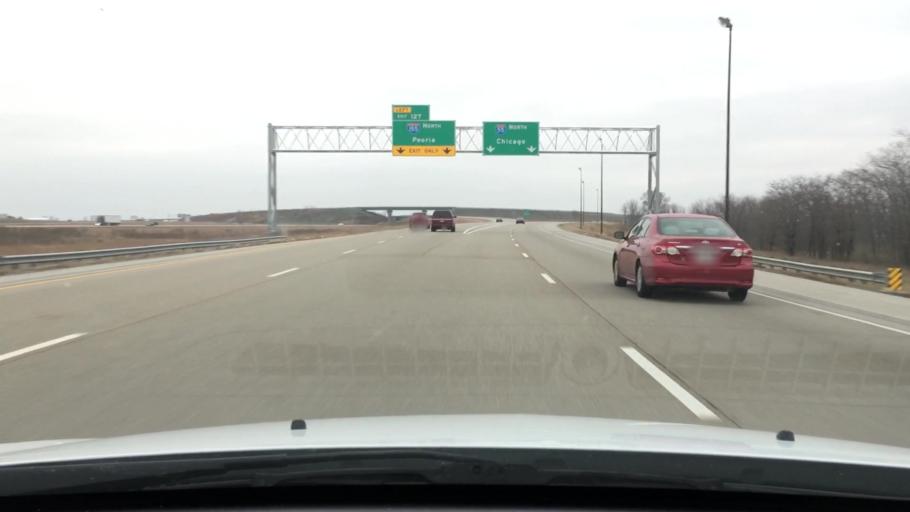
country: US
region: Illinois
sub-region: Logan County
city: Lincoln
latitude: 40.1719
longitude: -89.4170
